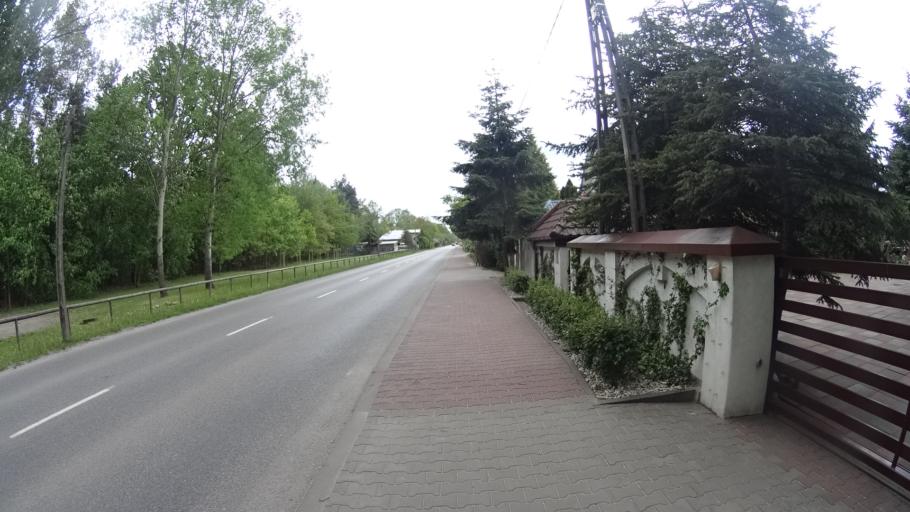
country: PL
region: Masovian Voivodeship
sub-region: Powiat warszawski zachodni
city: Babice
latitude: 52.2611
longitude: 20.8539
